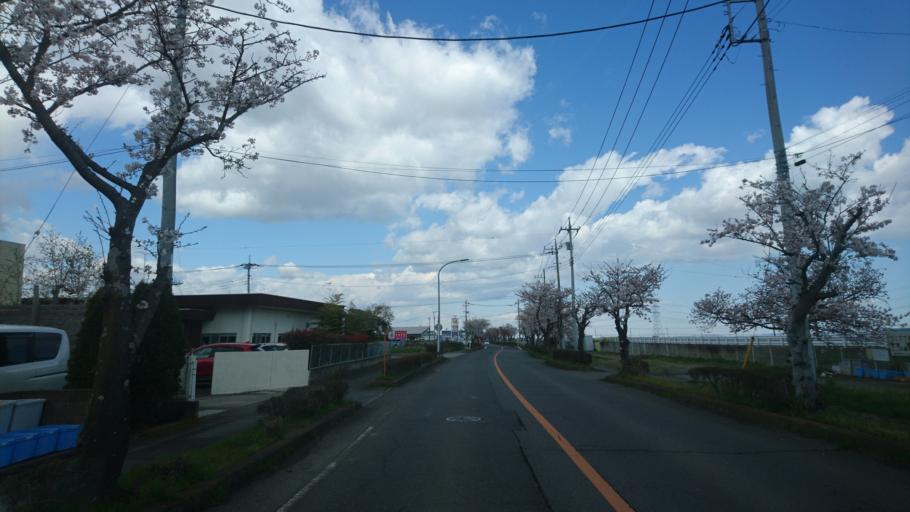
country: JP
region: Ibaraki
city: Ishige
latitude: 36.1165
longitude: 139.9778
